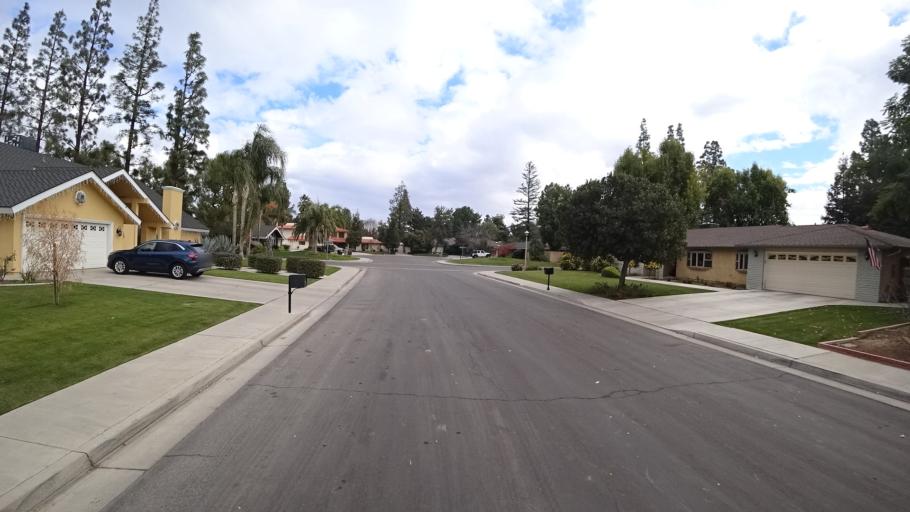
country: US
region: California
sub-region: Kern County
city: Greenacres
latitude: 35.3508
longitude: -119.0913
